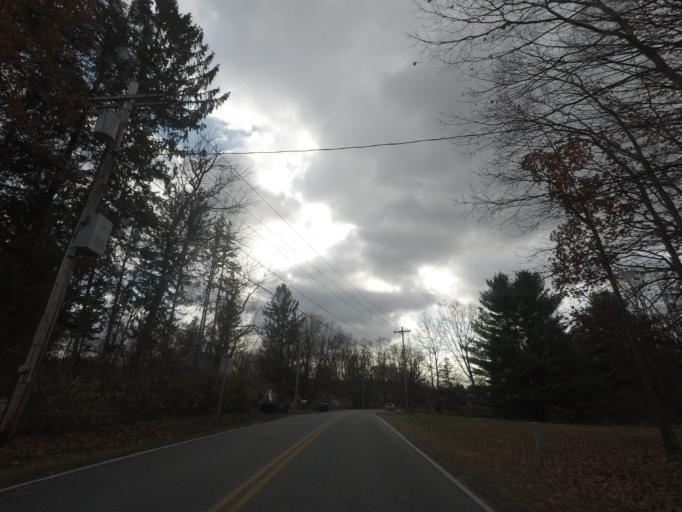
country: US
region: New York
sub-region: Saratoga County
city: Ballston Spa
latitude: 43.0048
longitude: -73.8083
